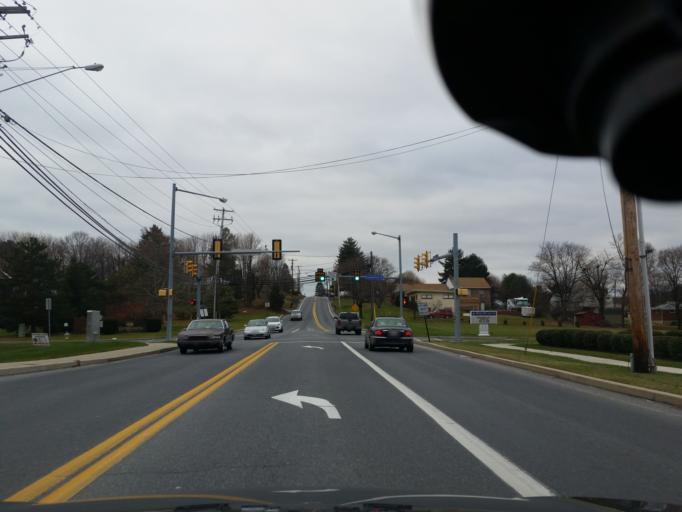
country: US
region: Pennsylvania
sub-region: Cumberland County
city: Enola
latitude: 40.2876
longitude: -76.9475
